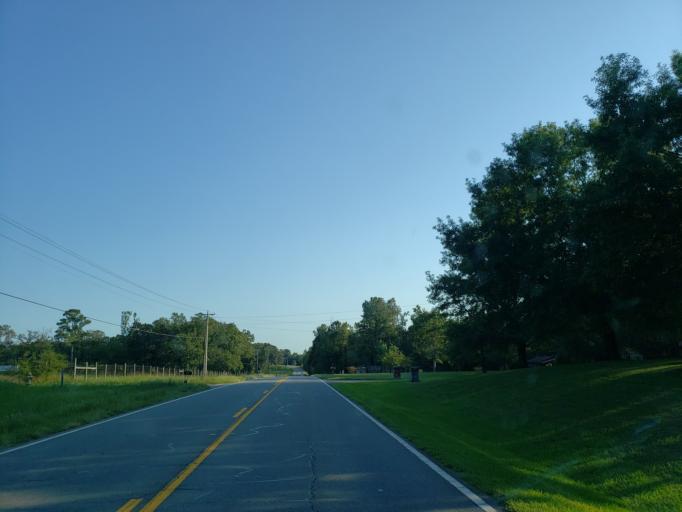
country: US
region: Georgia
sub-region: Murray County
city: Chatsworth
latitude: 34.7126
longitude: -84.8191
